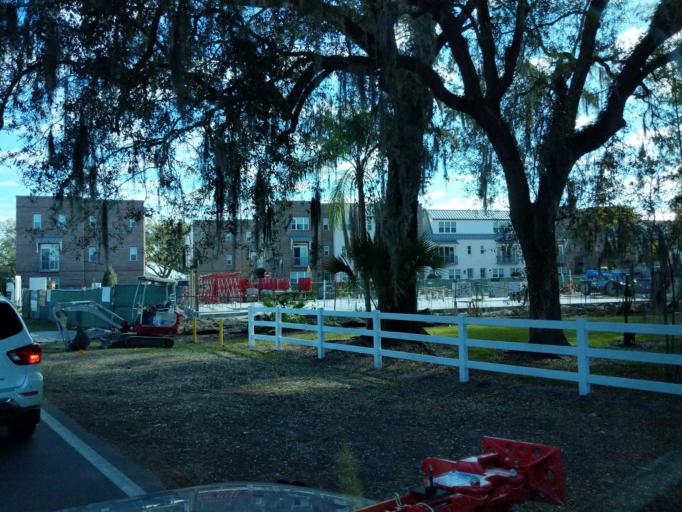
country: US
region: Florida
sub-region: Orange County
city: Winter Garden
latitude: 28.5642
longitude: -81.5925
